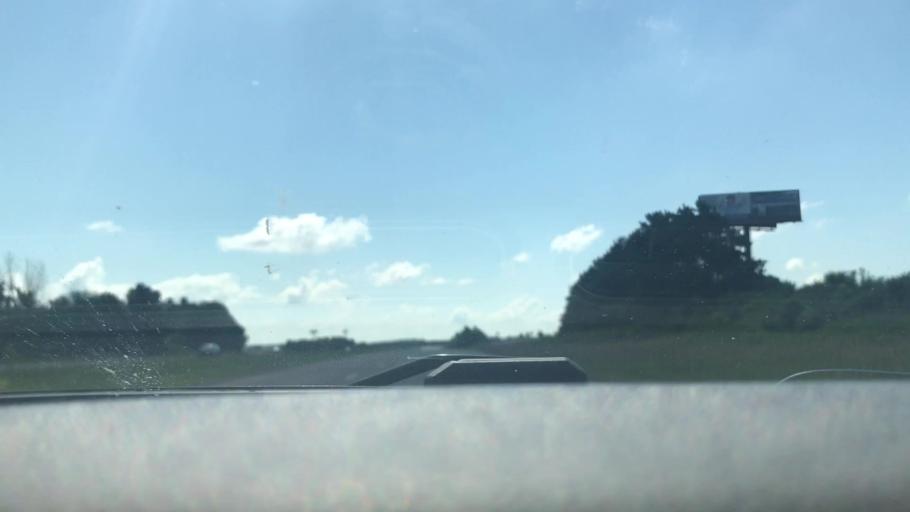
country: US
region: Wisconsin
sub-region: Chippewa County
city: Bloomer
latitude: 45.1034
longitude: -91.5100
